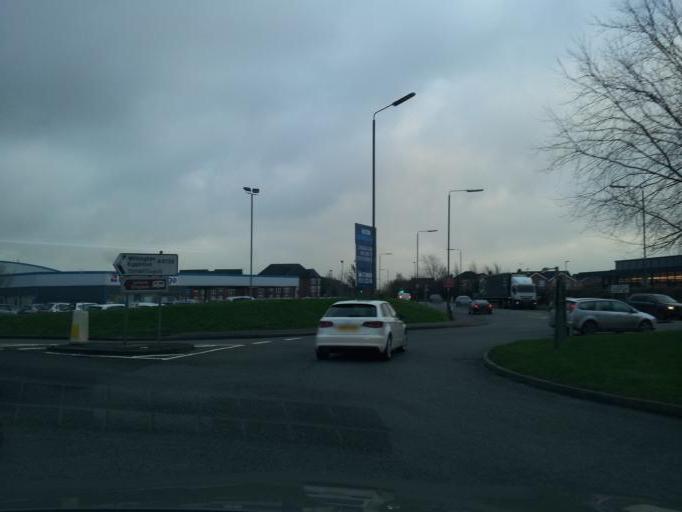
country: GB
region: England
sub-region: Derbyshire
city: Etwall
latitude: 52.8721
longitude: -1.6281
